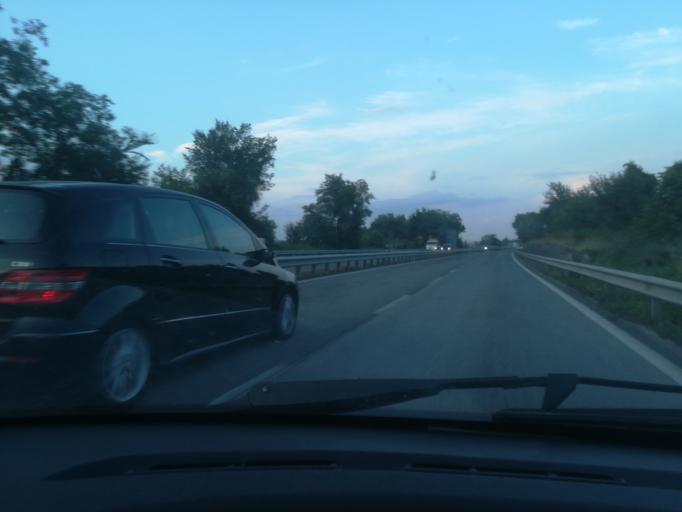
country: IT
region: The Marches
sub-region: Provincia di Macerata
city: Sforzacosta
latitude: 43.2435
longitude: 13.4181
